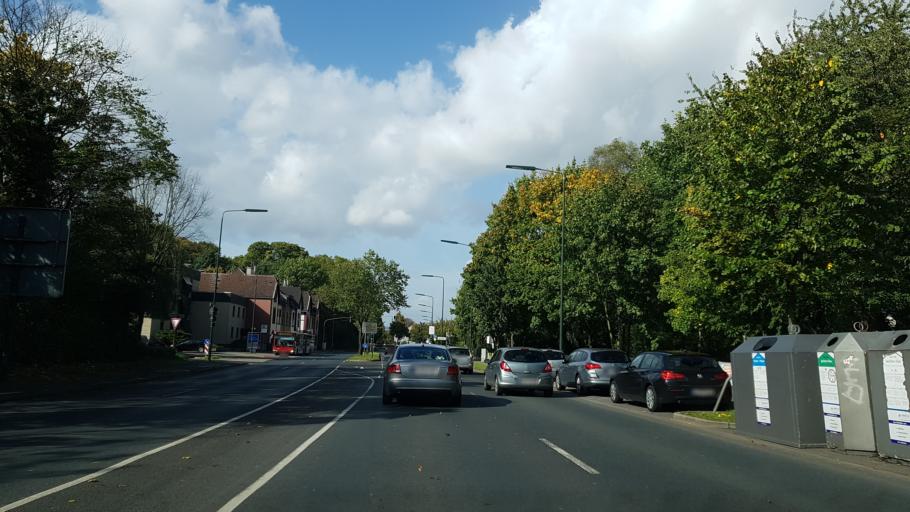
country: DE
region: North Rhine-Westphalia
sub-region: Regierungsbezirk Dusseldorf
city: Erkrath
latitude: 51.1925
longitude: 6.8573
